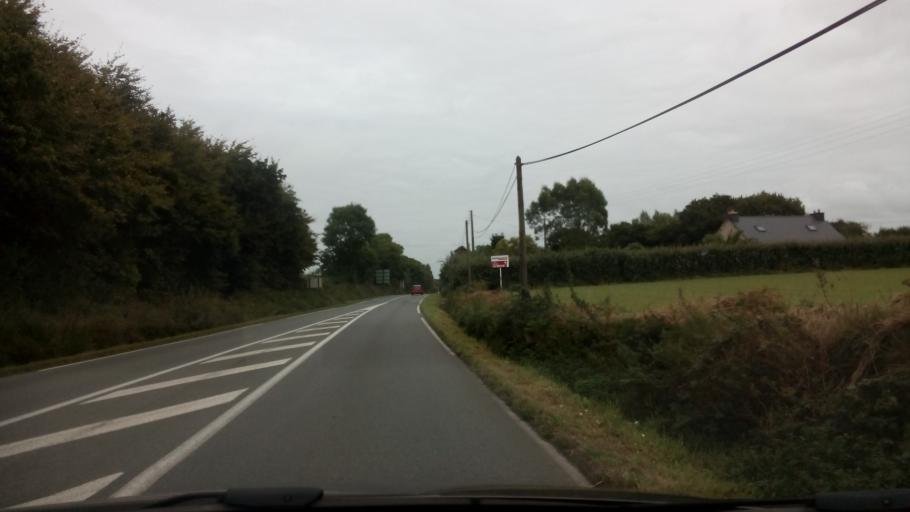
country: FR
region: Brittany
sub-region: Departement des Cotes-d'Armor
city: Ploumilliau
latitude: 48.6970
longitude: -3.5414
